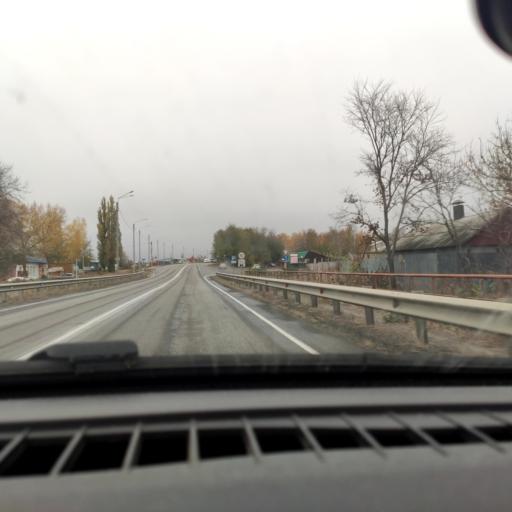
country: RU
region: Voronezj
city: Uryv-Pokrovka
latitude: 51.0420
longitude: 38.9824
